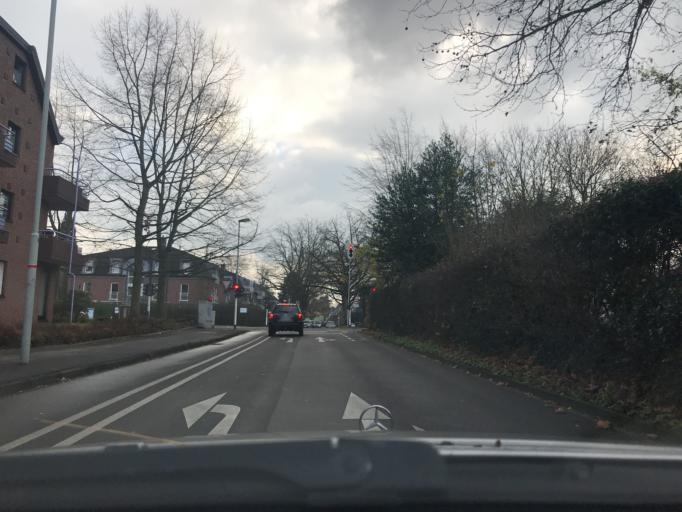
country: DE
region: North Rhine-Westphalia
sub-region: Regierungsbezirk Dusseldorf
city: Krefeld
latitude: 51.3451
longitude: 6.6135
